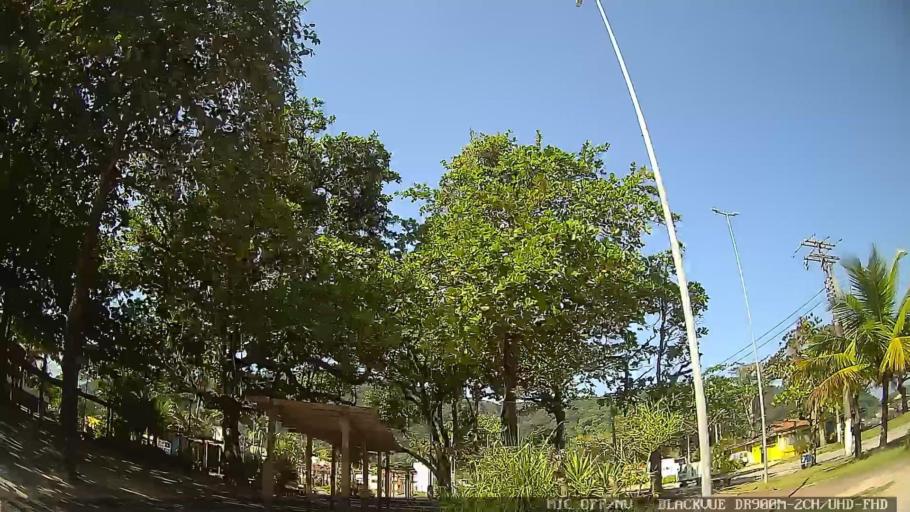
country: BR
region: Sao Paulo
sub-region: Guaruja
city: Guaruja
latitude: -24.0196
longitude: -46.2981
